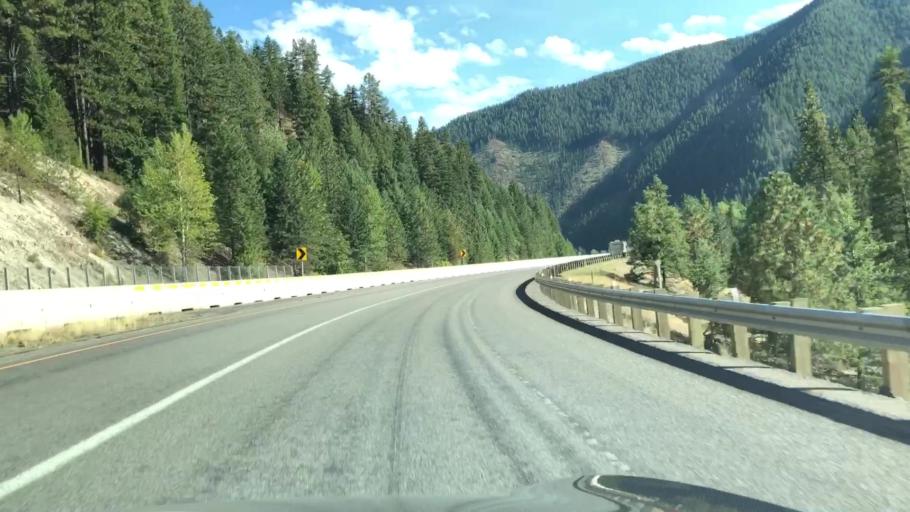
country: US
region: Montana
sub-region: Sanders County
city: Thompson Falls
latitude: 47.3115
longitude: -115.2099
